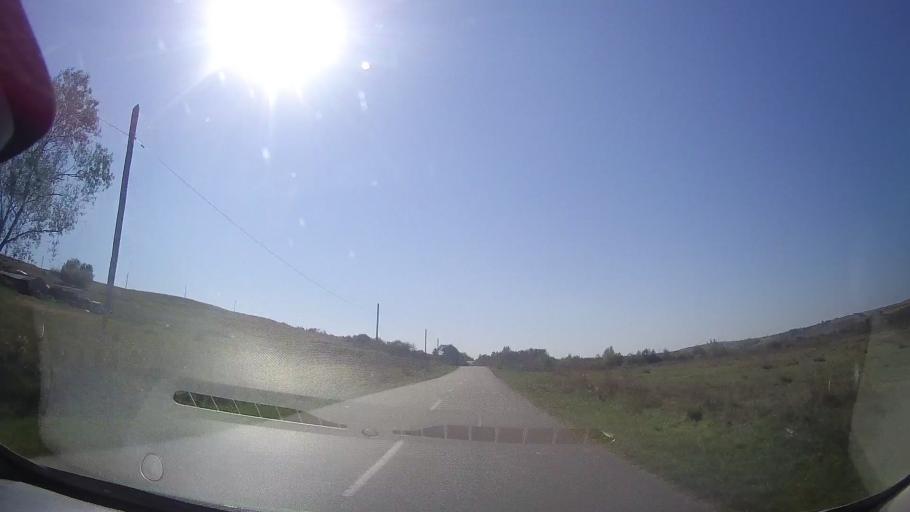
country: RO
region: Timis
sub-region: Comuna Bethausen
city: Bethausen
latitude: 45.8568
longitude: 21.9675
